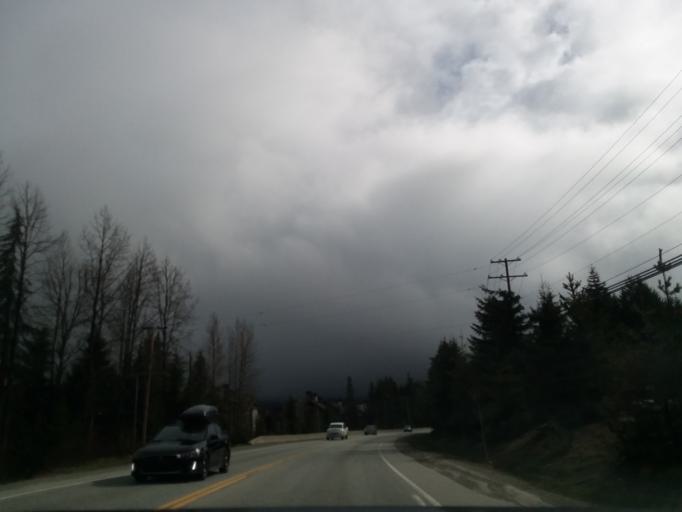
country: CA
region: British Columbia
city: Whistler
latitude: 50.1297
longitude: -122.9540
